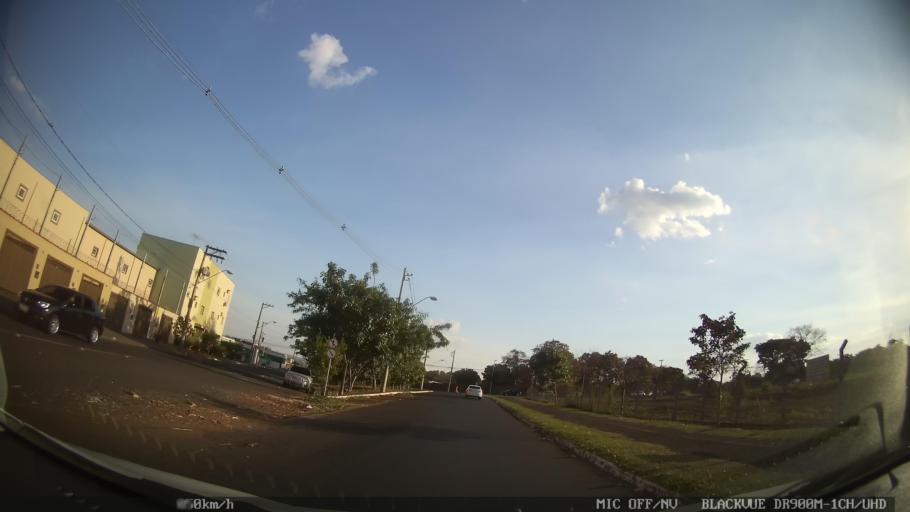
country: BR
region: Sao Paulo
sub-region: Ribeirao Preto
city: Ribeirao Preto
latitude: -21.1637
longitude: -47.8437
